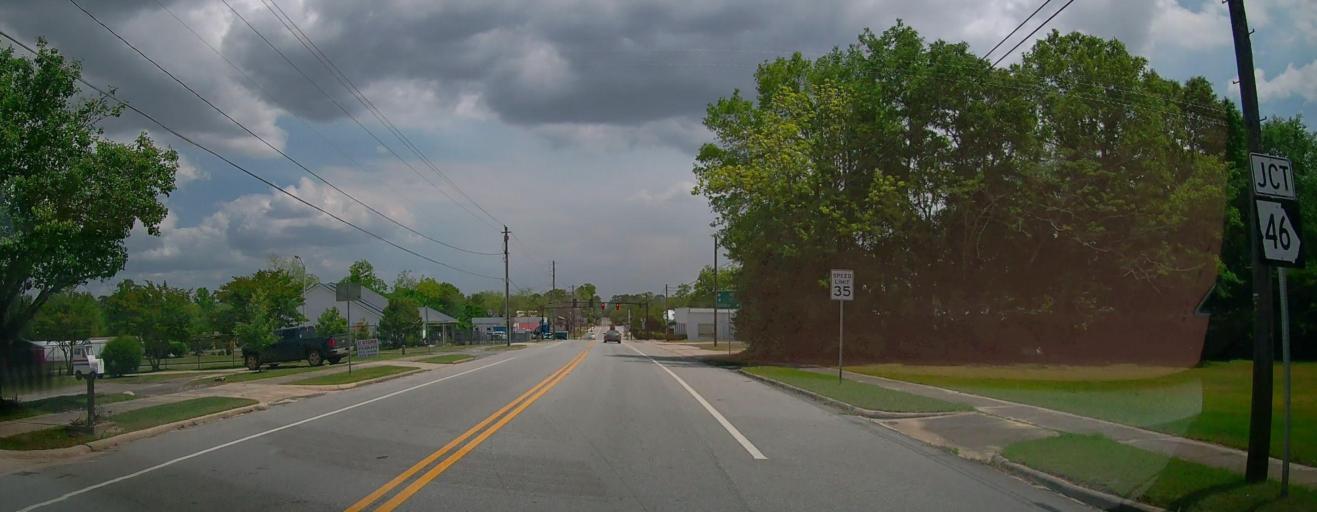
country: US
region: Georgia
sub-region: Treutlen County
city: Soperton
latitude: 32.3810
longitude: -82.5941
